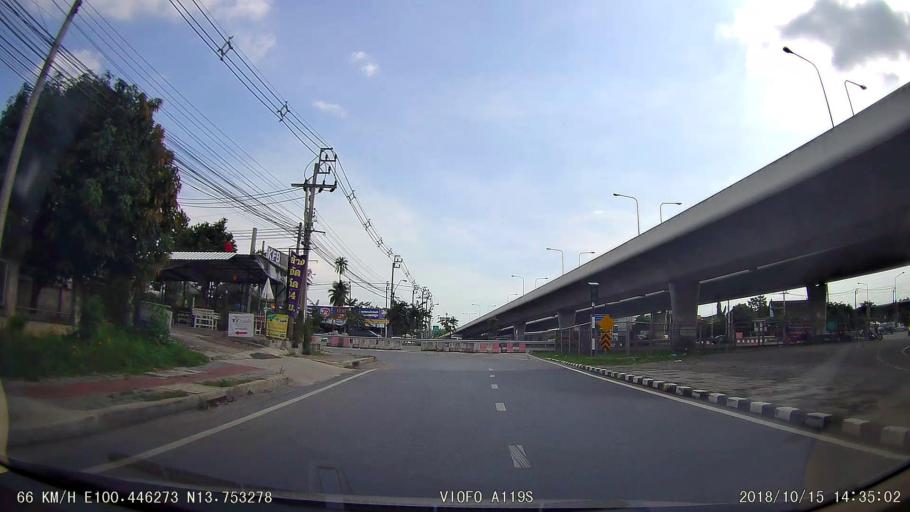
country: TH
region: Bangkok
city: Taling Chan
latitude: 13.7530
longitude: 100.4464
